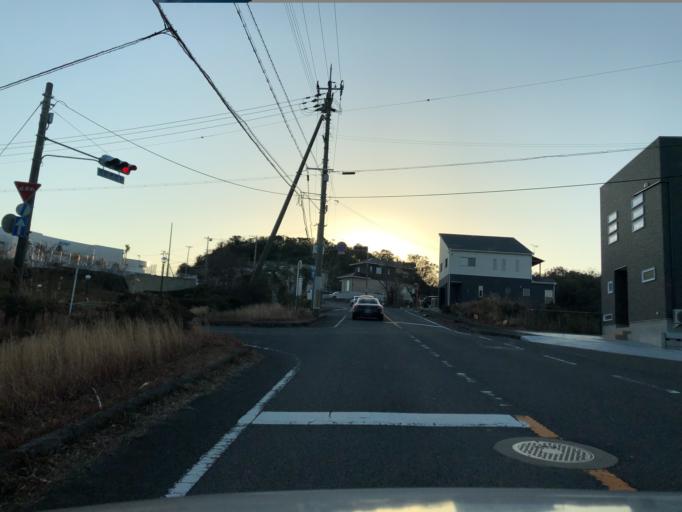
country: JP
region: Wakayama
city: Tanabe
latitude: 33.6694
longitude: 135.3696
